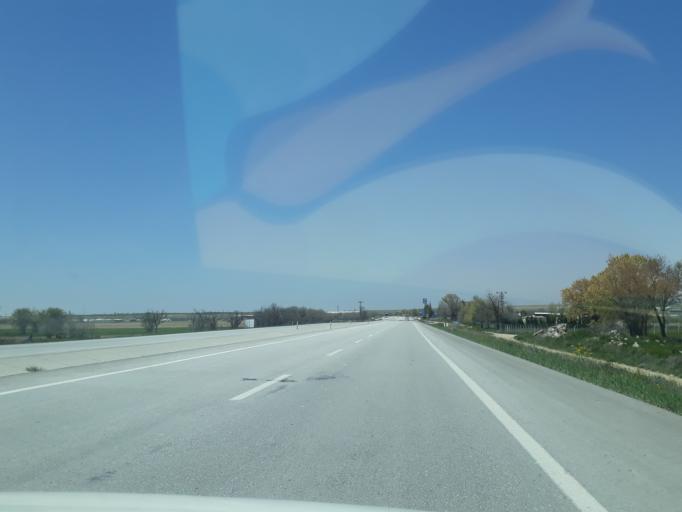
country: TR
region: Konya
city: Karapinar
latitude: 37.7161
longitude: 33.4955
